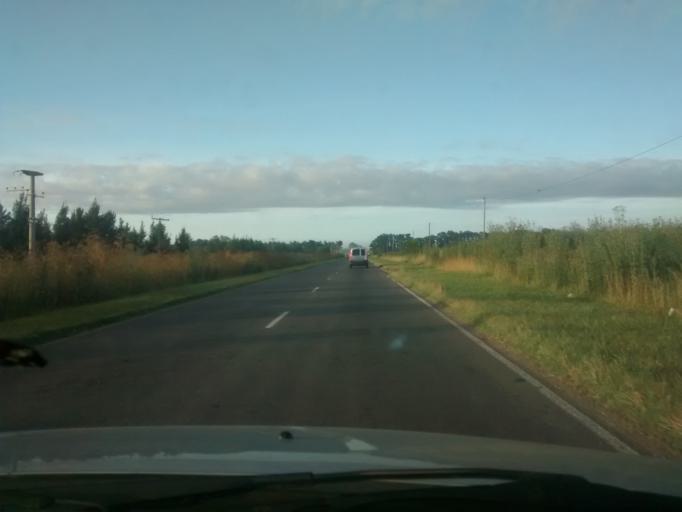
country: AR
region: Buenos Aires
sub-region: Partido de Brandsen
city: Brandsen
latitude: -35.1237
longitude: -58.1905
